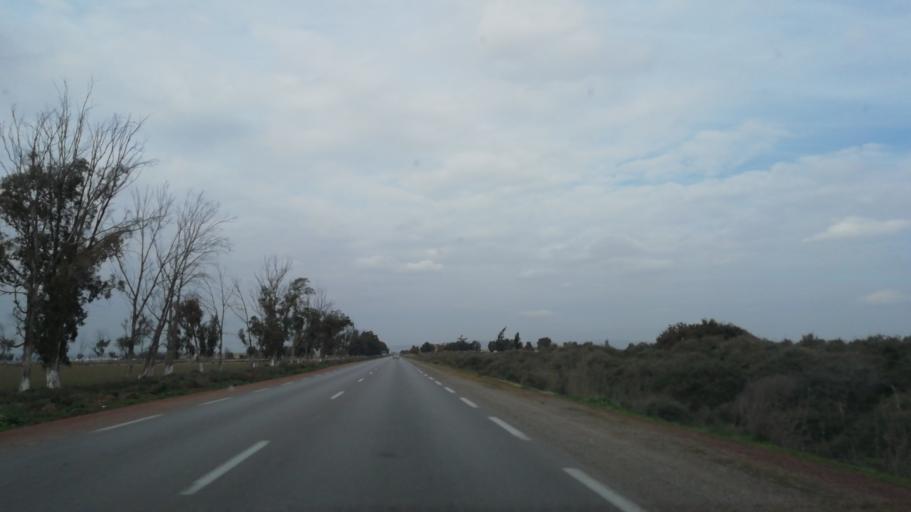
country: DZ
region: Mostaganem
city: Mostaganem
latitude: 35.6783
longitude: 0.0571
